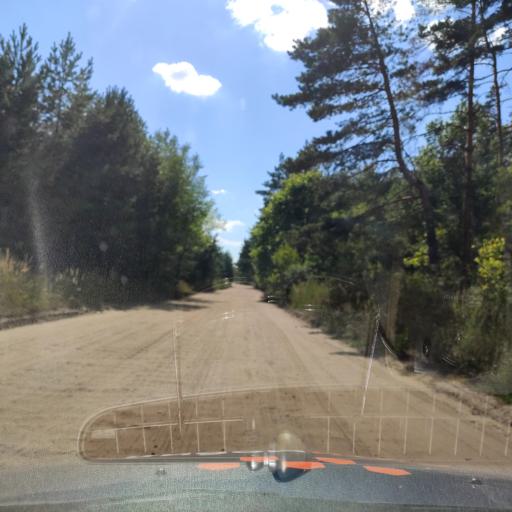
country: RU
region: Voronezj
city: Somovo
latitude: 51.7194
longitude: 39.3871
